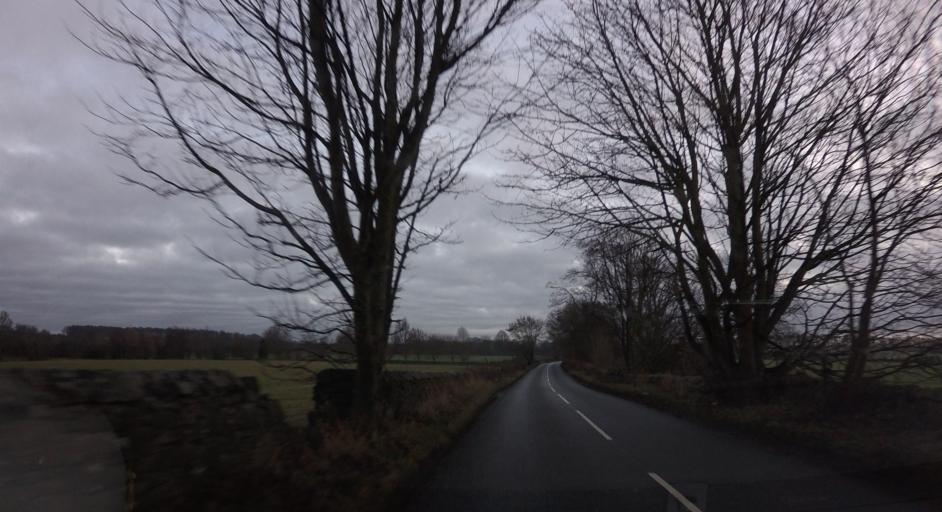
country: GB
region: Scotland
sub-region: Fife
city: Crossford
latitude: 56.0575
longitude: -3.4925
